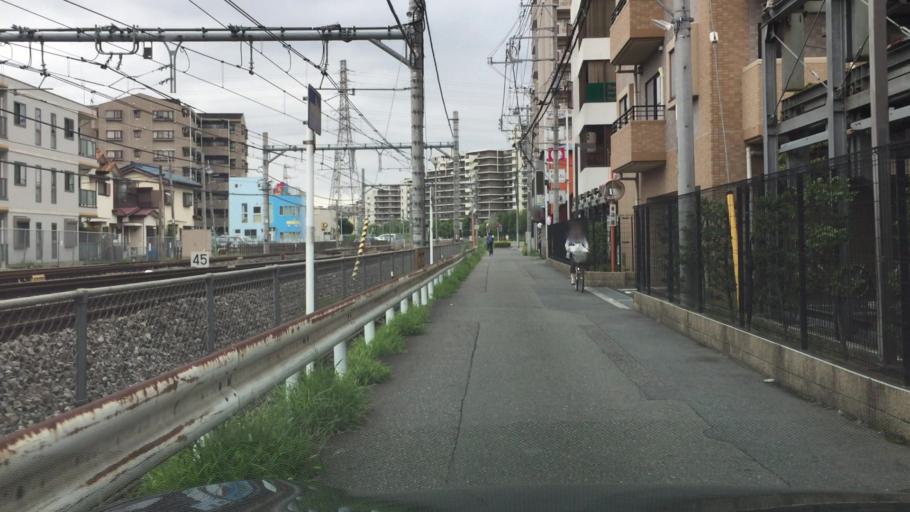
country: JP
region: Saitama
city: Ageoshimo
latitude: 35.9385
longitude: 139.6097
